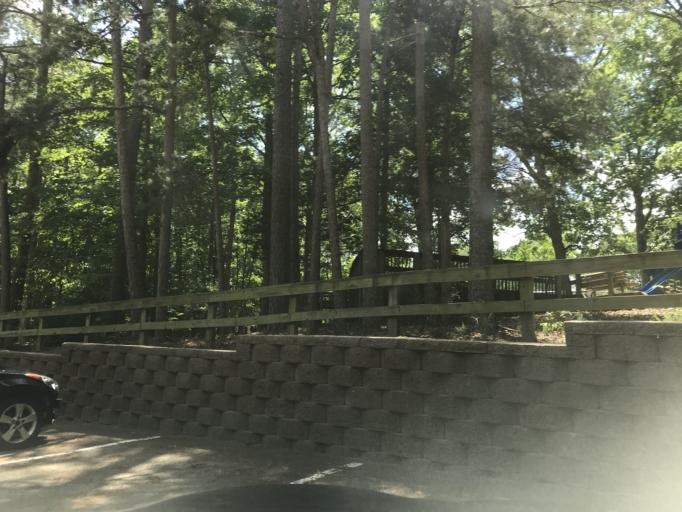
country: US
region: North Carolina
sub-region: Wake County
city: West Raleigh
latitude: 35.8593
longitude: -78.6291
